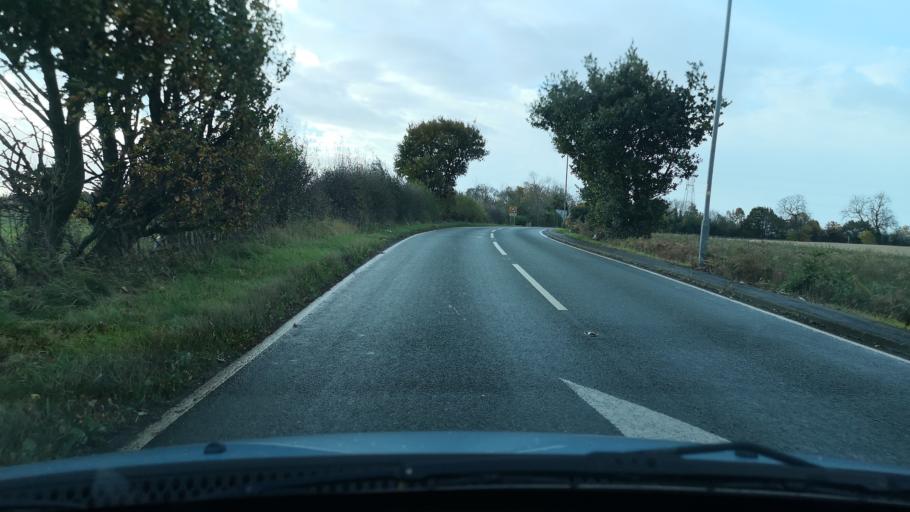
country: GB
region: England
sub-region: City and Borough of Wakefield
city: Ryhill
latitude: 53.6154
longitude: -1.4248
